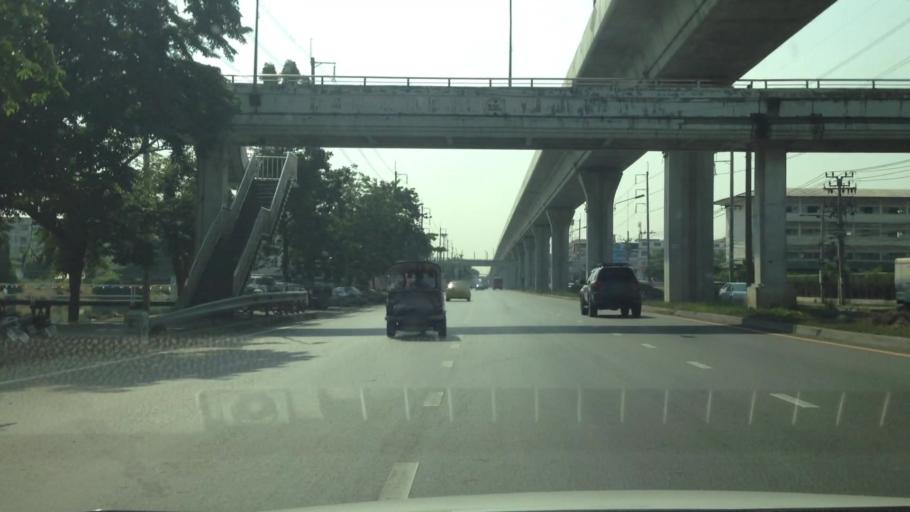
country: TH
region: Samut Prakan
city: Samut Prakan
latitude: 13.5663
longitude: 100.6084
